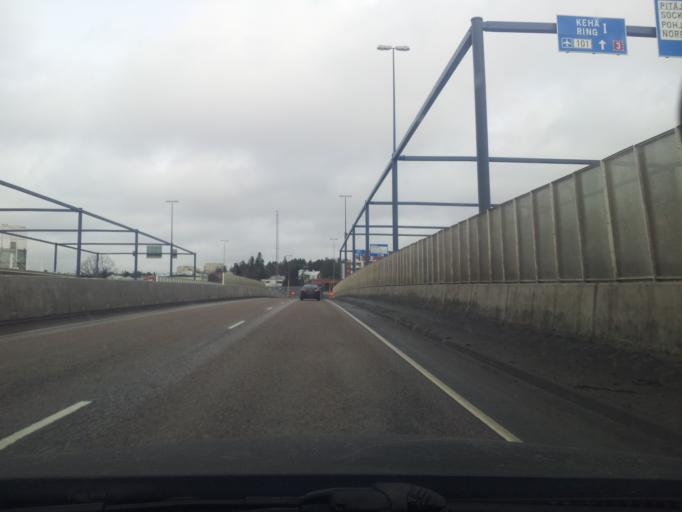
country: FI
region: Uusimaa
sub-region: Helsinki
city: Teekkarikylae
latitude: 60.2187
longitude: 24.8164
